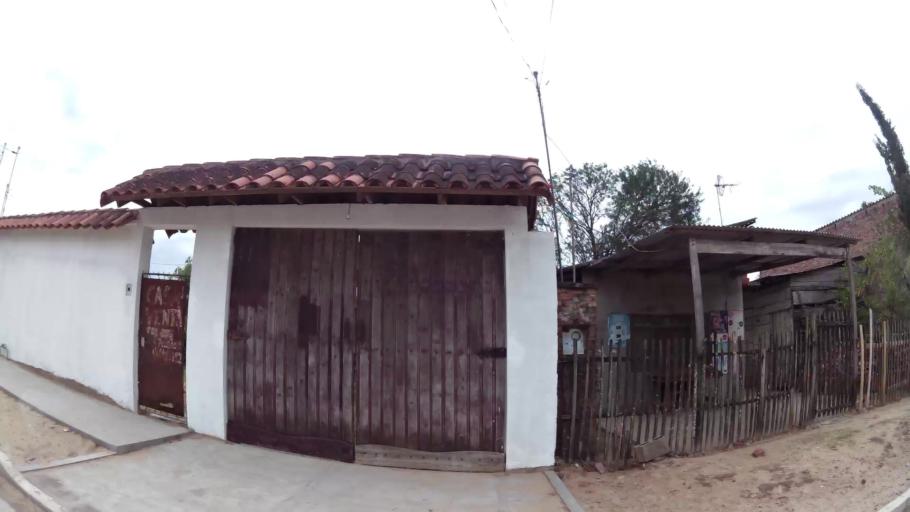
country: BO
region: Santa Cruz
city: Santa Cruz de la Sierra
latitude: -17.7372
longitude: -63.1923
